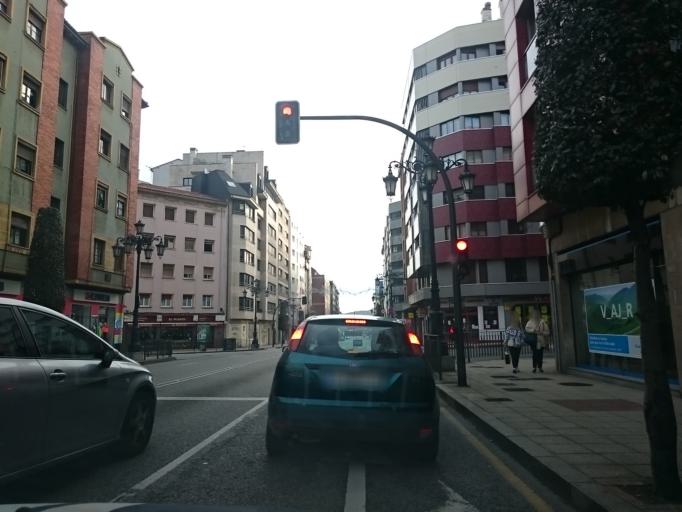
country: ES
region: Asturias
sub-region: Province of Asturias
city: Oviedo
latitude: 43.3605
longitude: -5.8387
